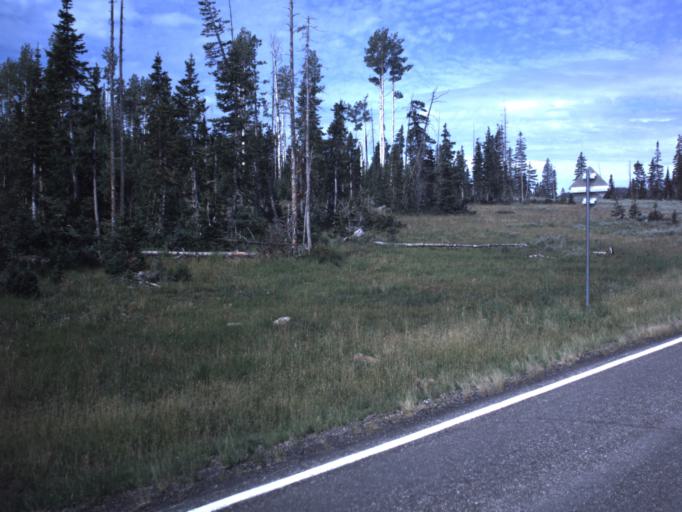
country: US
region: Utah
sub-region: Iron County
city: Parowan
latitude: 37.5682
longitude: -112.7930
